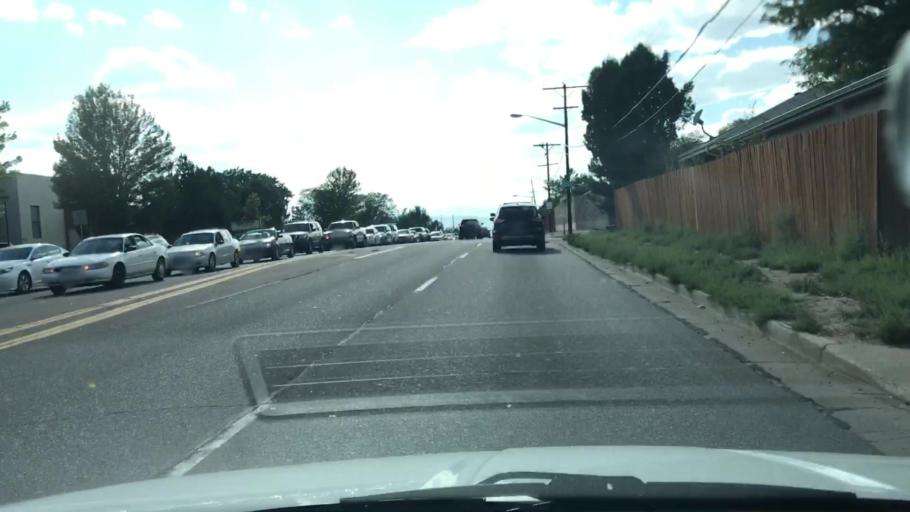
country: US
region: Colorado
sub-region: Arapahoe County
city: Cherry Hills Village
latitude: 39.6531
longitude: -104.9322
